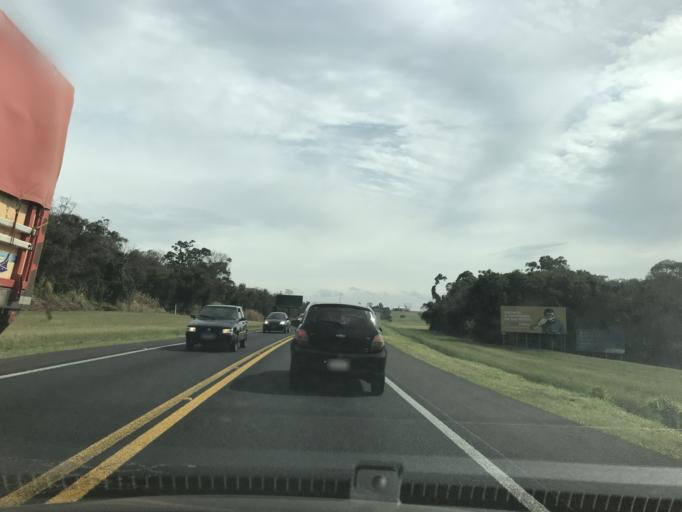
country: BR
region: Parana
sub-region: Matelandia
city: Matelandia
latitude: -25.1129
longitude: -53.7729
